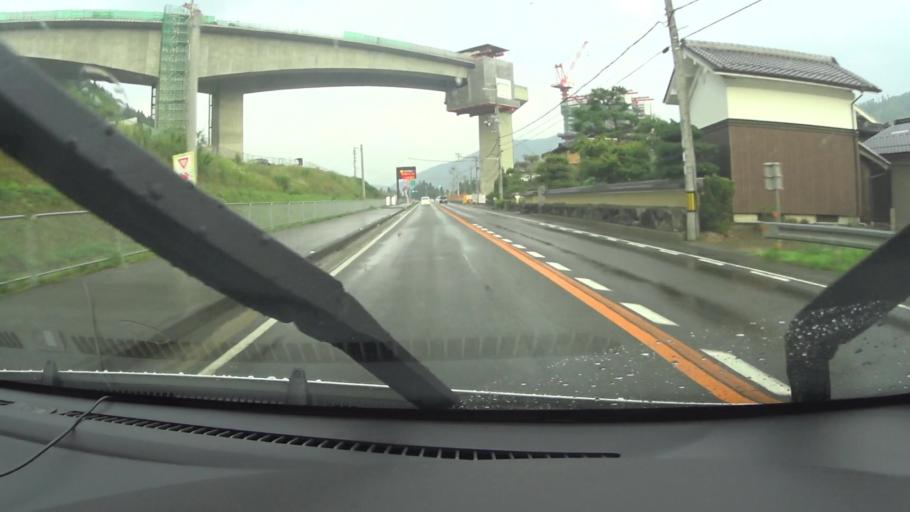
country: JP
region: Kyoto
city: Ayabe
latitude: 35.2772
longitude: 135.3369
